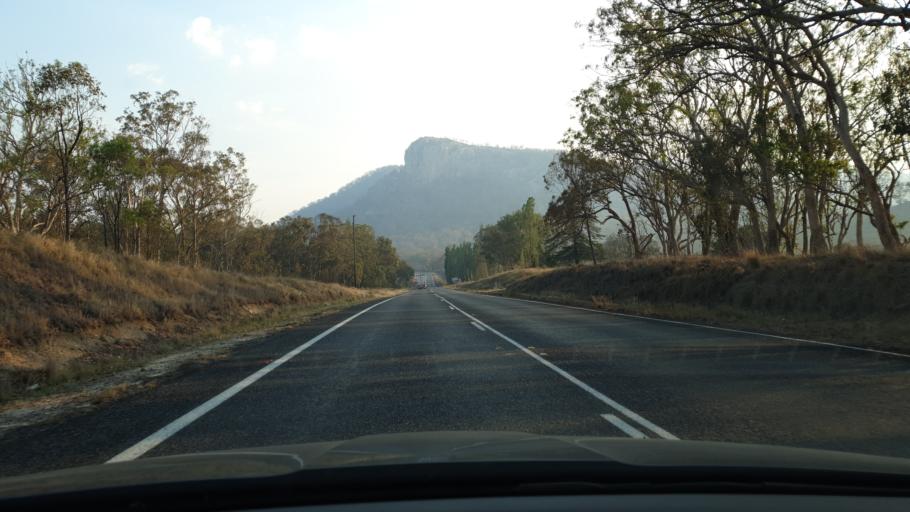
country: AU
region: New South Wales
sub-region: Tenterfield Municipality
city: Carrolls Creek
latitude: -29.1555
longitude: 152.0013
